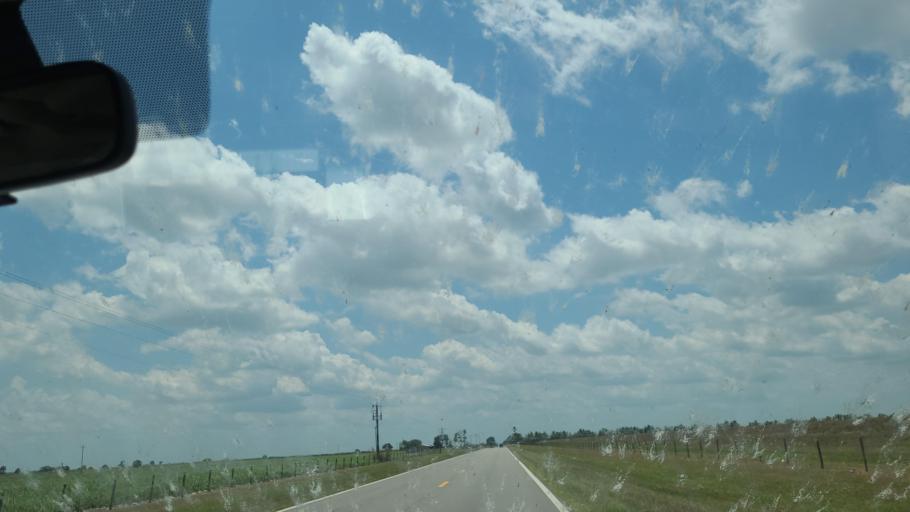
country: US
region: Florida
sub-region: Okeechobee County
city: Okeechobee
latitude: 27.3046
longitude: -81.0542
